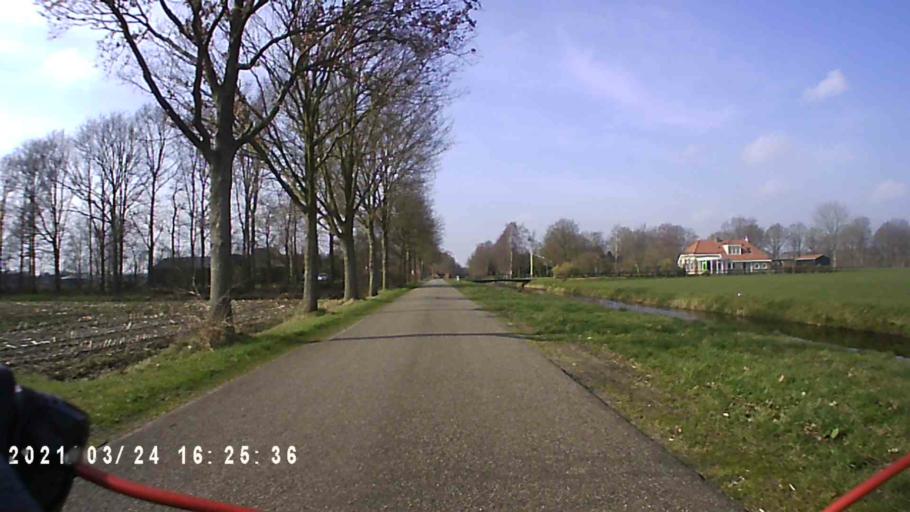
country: NL
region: Friesland
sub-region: Gemeente Smallingerland
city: Drachtstercompagnie
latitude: 53.0619
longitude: 6.2691
